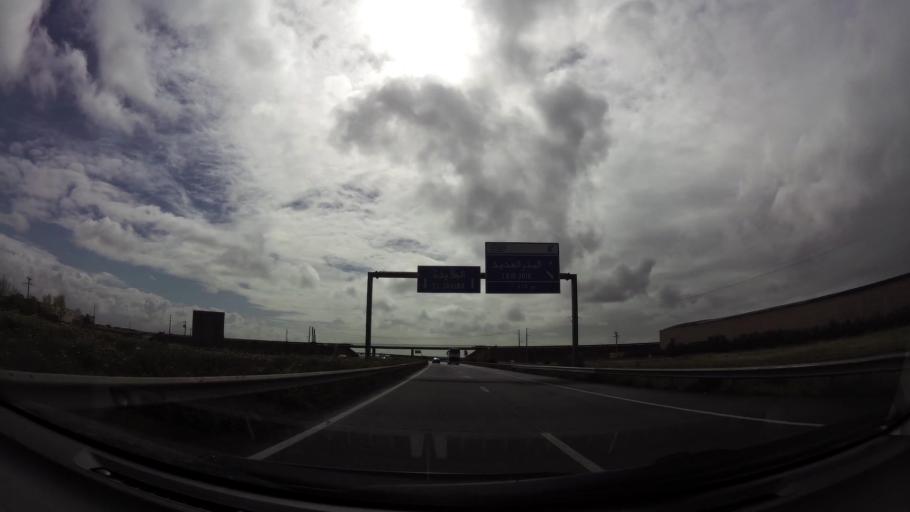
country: MA
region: Grand Casablanca
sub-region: Nouaceur
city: Dar Bouazza
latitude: 33.3525
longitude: -7.9917
